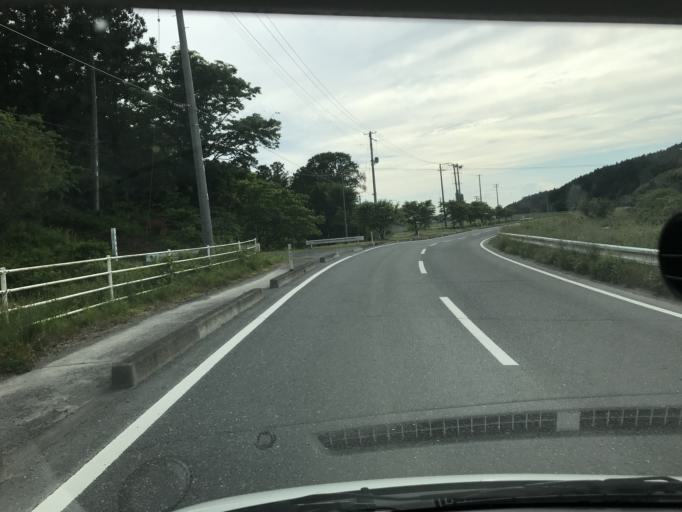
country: JP
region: Miyagi
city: Wakuya
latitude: 38.6562
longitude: 141.3059
